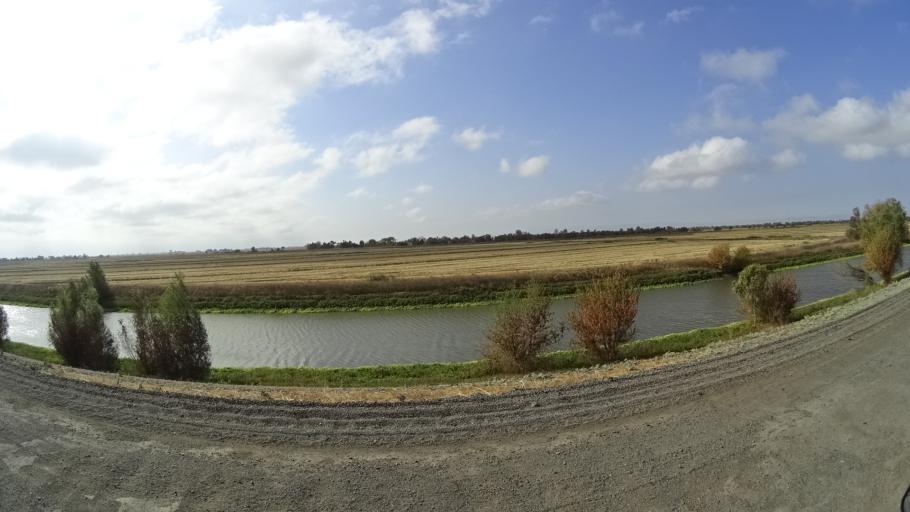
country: US
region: California
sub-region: Yolo County
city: Woodland
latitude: 38.8174
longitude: -121.7841
